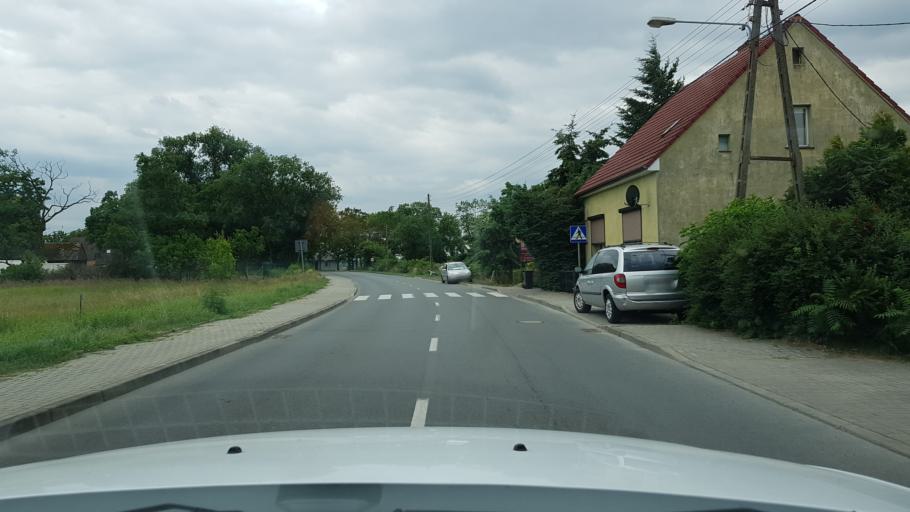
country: PL
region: Lubusz
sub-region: Powiat gorzowski
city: Kostrzyn nad Odra
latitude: 52.6114
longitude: 14.6195
